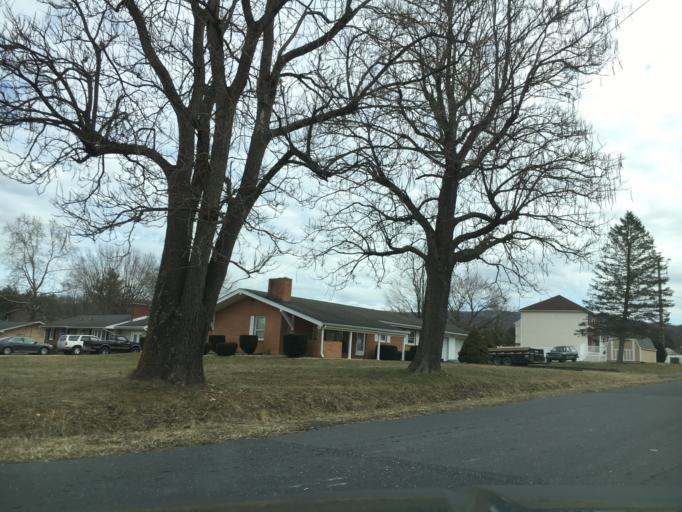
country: US
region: Virginia
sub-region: Augusta County
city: Crimora
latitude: 38.1397
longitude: -78.8444
